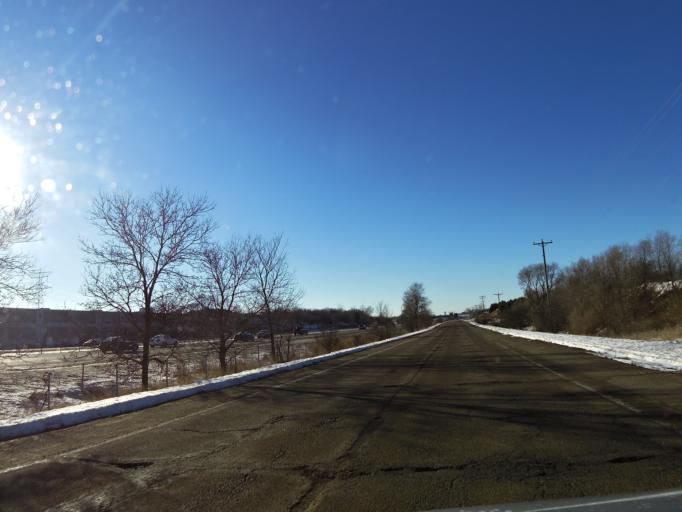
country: US
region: Minnesota
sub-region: Washington County
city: Lakeland
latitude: 44.9491
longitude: -92.8293
